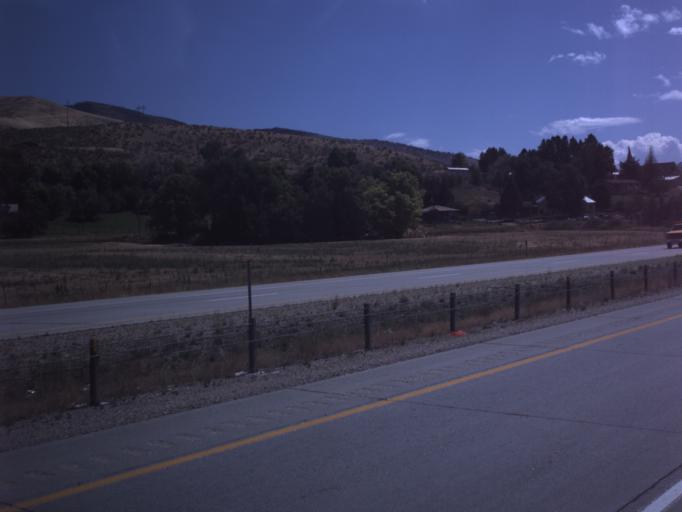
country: US
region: Utah
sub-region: Morgan County
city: Morgan
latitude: 41.0693
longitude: -111.7146
